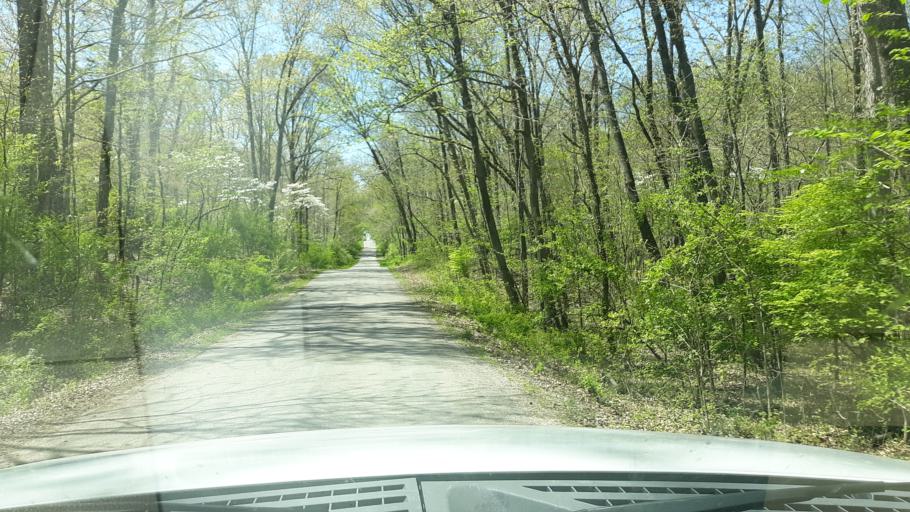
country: US
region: Illinois
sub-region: Saline County
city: Harrisburg
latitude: 37.8596
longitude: -88.6271
